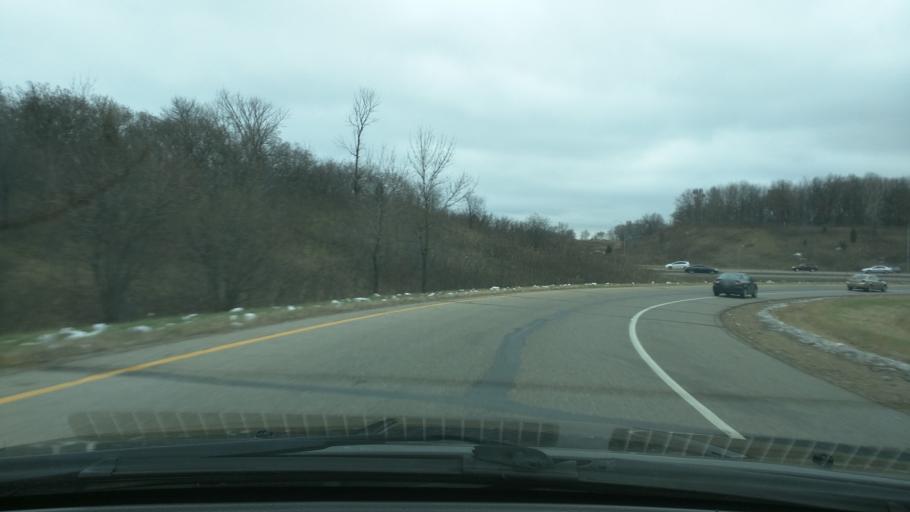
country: US
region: Minnesota
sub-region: Dakota County
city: Mendota Heights
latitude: 44.8640
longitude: -93.1267
